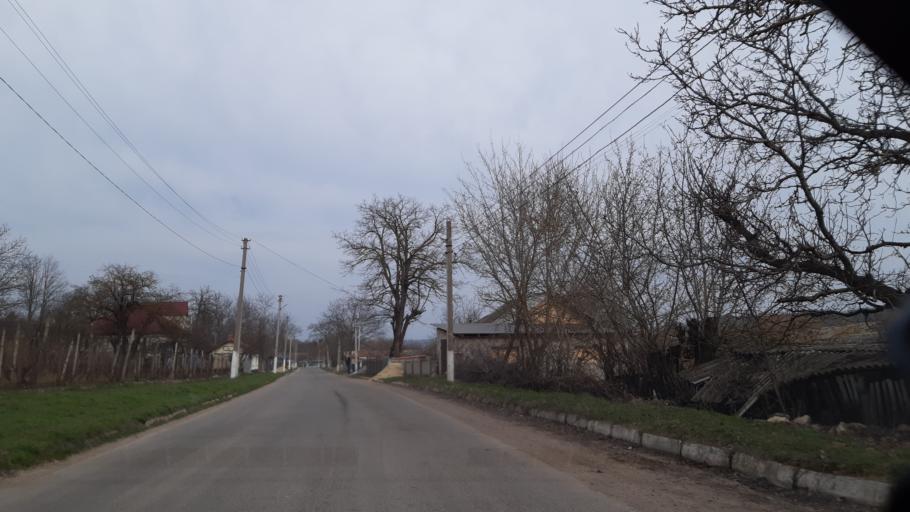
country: MD
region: Soldanesti
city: Soldanesti
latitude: 47.6857
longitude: 28.7520
